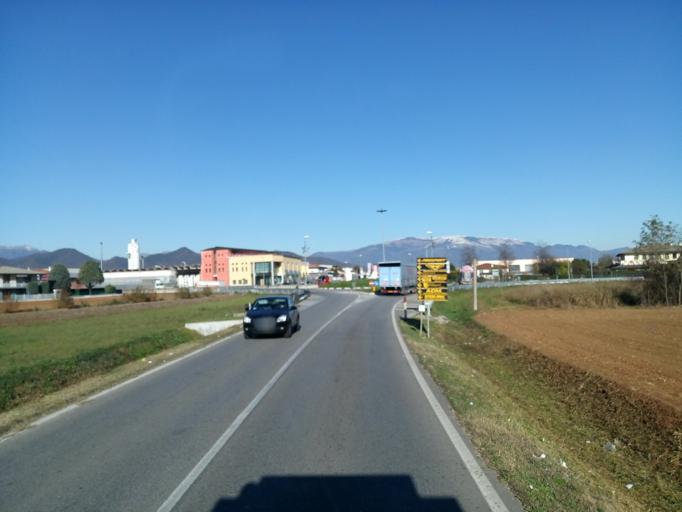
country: IT
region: Veneto
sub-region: Provincia di Treviso
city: Caerano di San Marco
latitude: 45.7783
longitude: 11.9935
